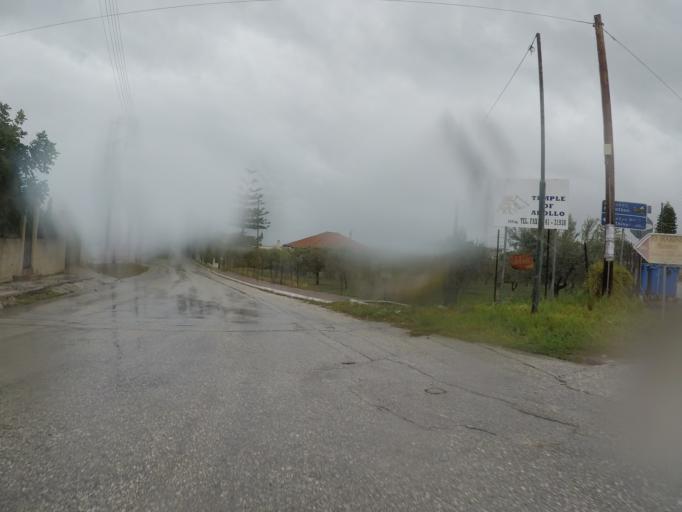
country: GR
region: Peloponnese
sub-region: Nomos Korinthias
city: Arkhaia Korinthos
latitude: 37.9084
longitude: 22.8849
